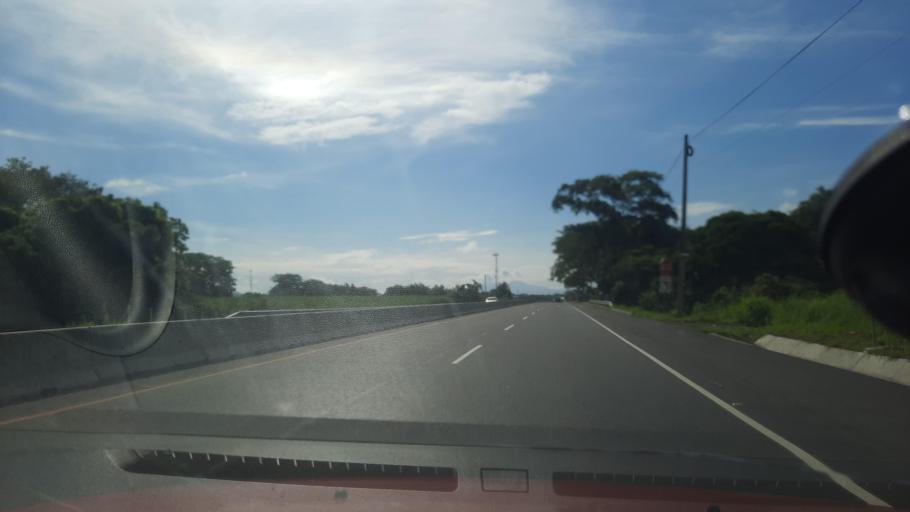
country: SV
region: La Paz
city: Santiago Nonualco
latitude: 13.4871
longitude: -88.9643
